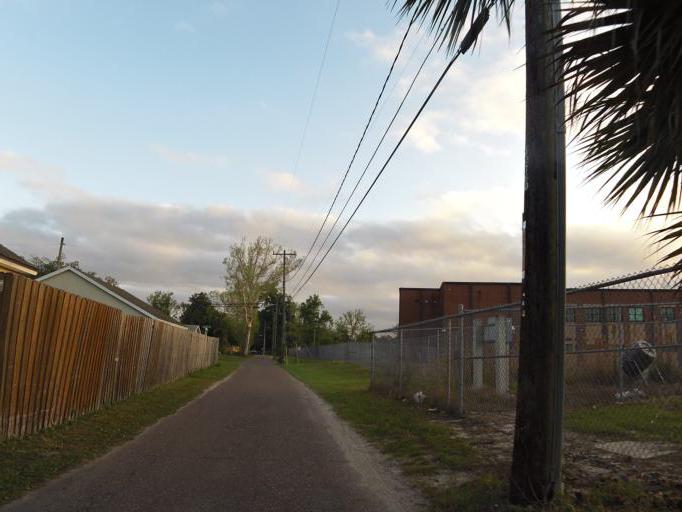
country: US
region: Florida
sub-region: Duval County
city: Jacksonville
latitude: 30.4681
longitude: -81.6303
